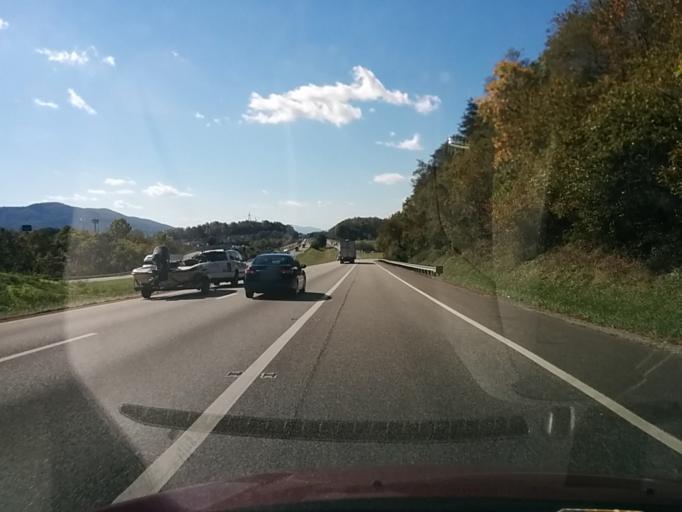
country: US
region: Virginia
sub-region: Botetourt County
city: Daleville
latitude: 37.3944
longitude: -79.9018
